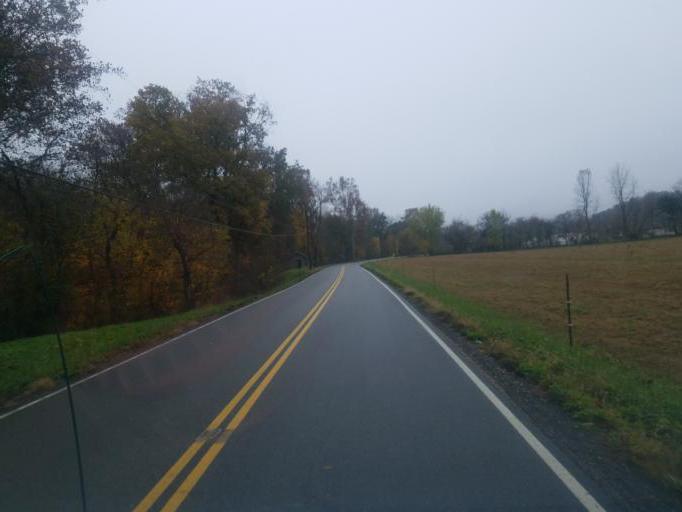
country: US
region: Ohio
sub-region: Morgan County
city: McConnelsville
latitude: 39.6331
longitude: -81.8380
